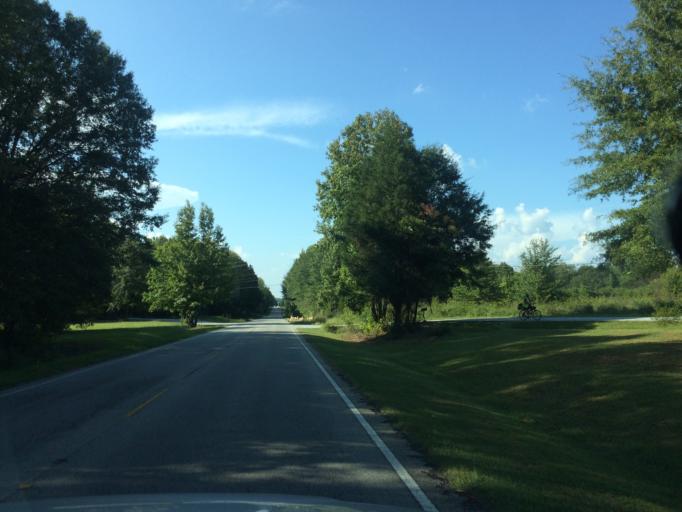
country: US
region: South Carolina
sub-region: Laurens County
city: Laurens
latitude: 34.5530
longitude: -82.0751
